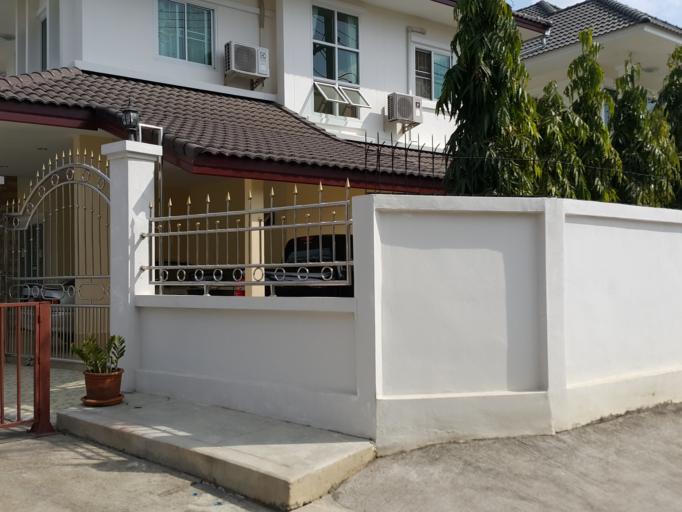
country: TH
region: Chiang Mai
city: Saraphi
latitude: 18.7502
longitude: 99.0085
